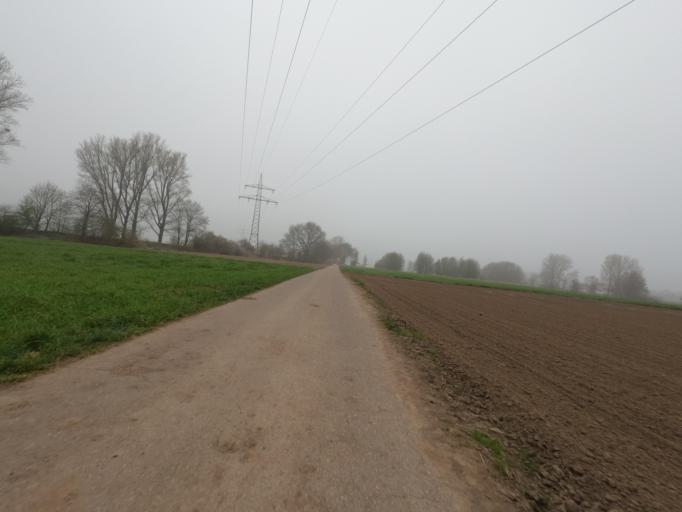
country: DE
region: North Rhine-Westphalia
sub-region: Regierungsbezirk Koln
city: Wassenberg
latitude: 51.0693
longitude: 6.1516
